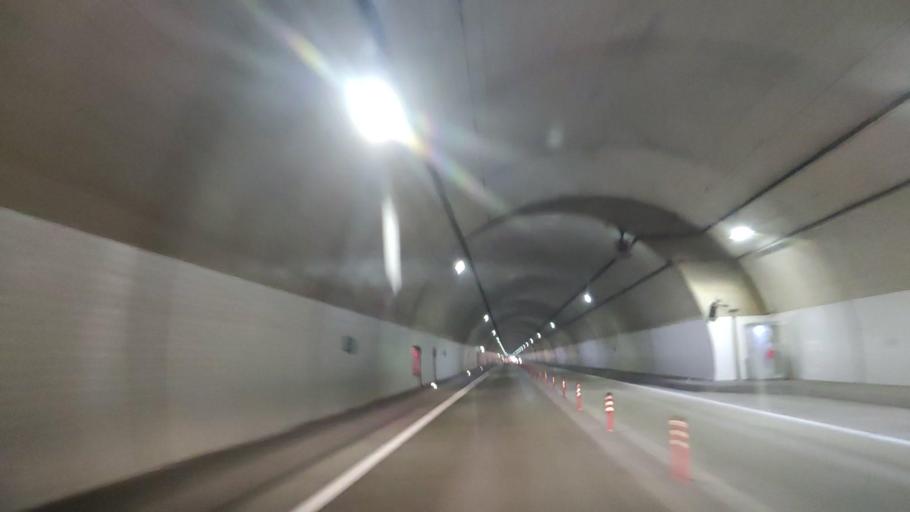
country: JP
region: Akita
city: Odate
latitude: 40.3499
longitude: 140.6752
